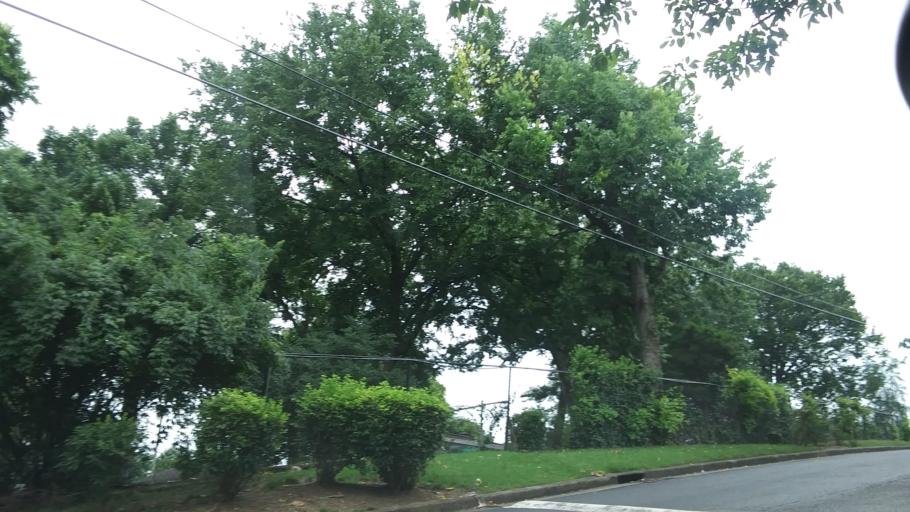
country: US
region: Tennessee
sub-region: Davidson County
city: Belle Meade
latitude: 36.1450
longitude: -86.8550
